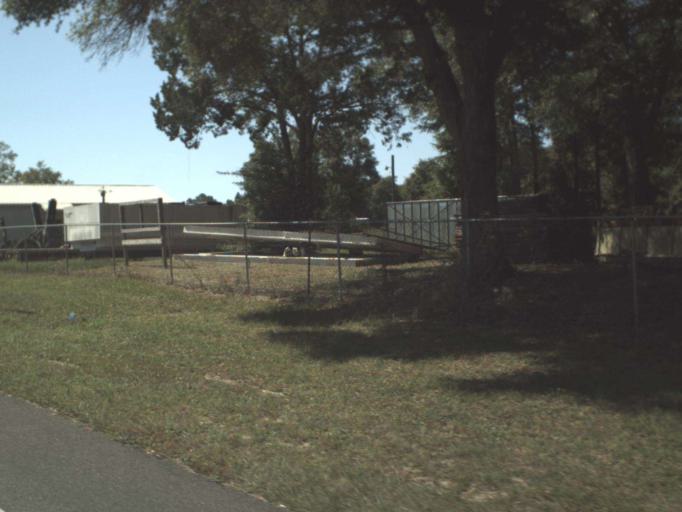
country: US
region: Florida
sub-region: Walton County
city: DeFuniak Springs
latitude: 30.7293
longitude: -86.1147
